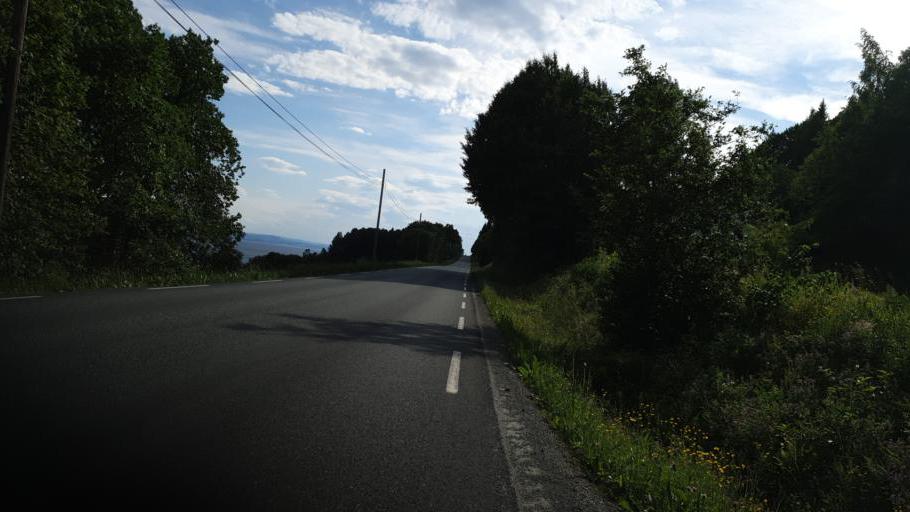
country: NO
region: Sor-Trondelag
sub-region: Trondheim
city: Trondheim
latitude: 63.5611
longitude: 10.3184
